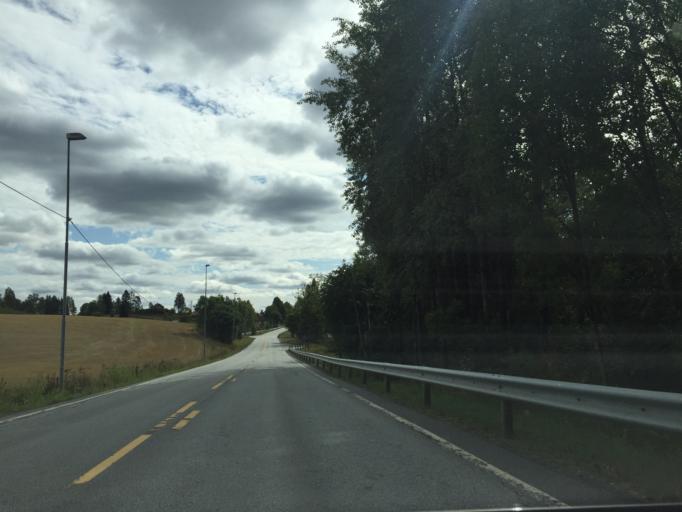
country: NO
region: Ostfold
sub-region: Hobol
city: Elvestad
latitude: 59.6313
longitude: 10.9385
